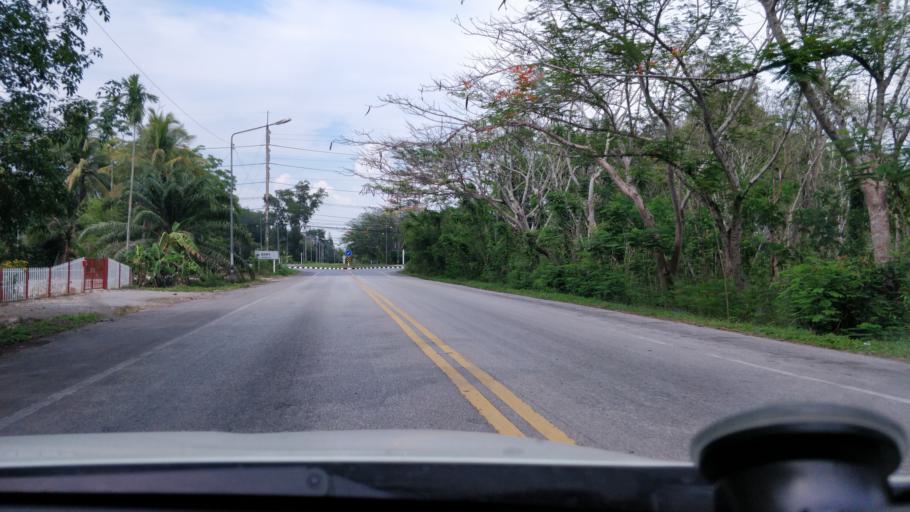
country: TH
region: Surat Thani
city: Ban Na Doem
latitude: 8.9355
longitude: 99.2638
